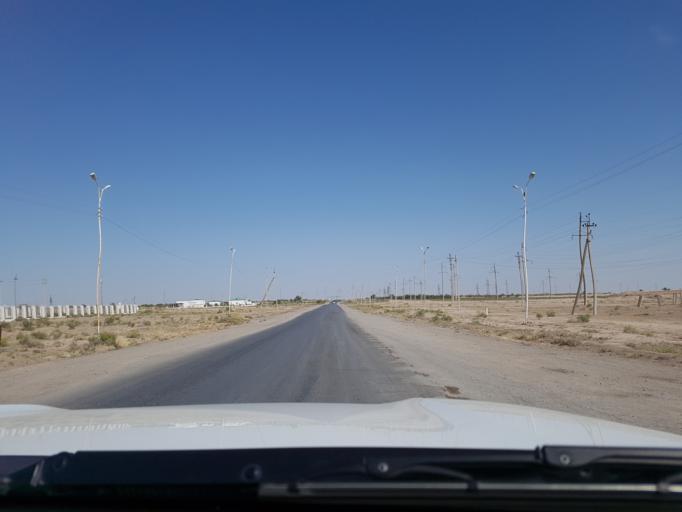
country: IR
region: Razavi Khorasan
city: Sarakhs
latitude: 36.5239
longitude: 61.2284
